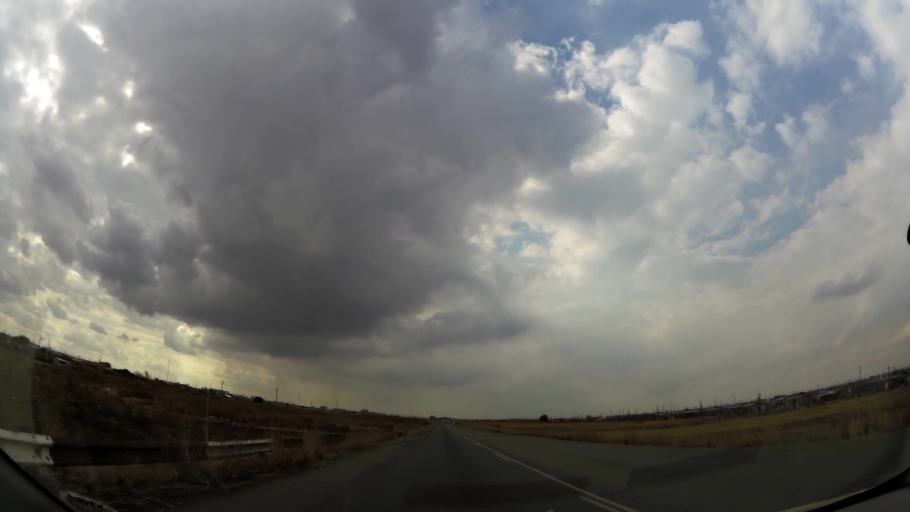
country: ZA
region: Orange Free State
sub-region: Fezile Dabi District Municipality
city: Sasolburg
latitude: -26.8646
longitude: 27.8878
